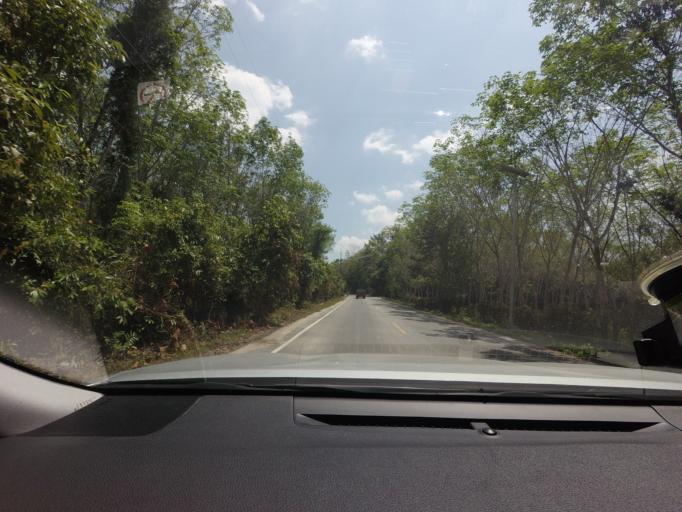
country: TH
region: Narathiwat
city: Rueso
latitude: 6.3888
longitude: 101.5043
